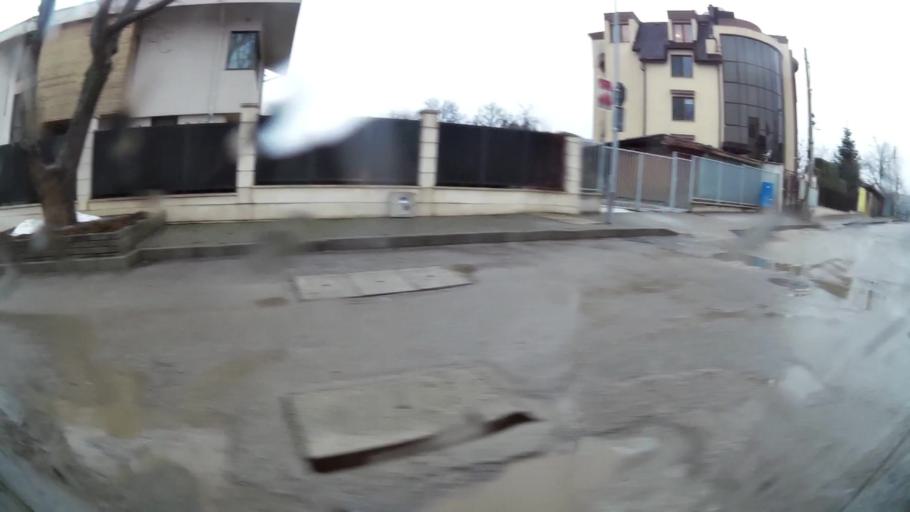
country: BG
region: Sofia-Capital
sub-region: Stolichna Obshtina
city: Sofia
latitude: 42.6489
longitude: 23.3190
